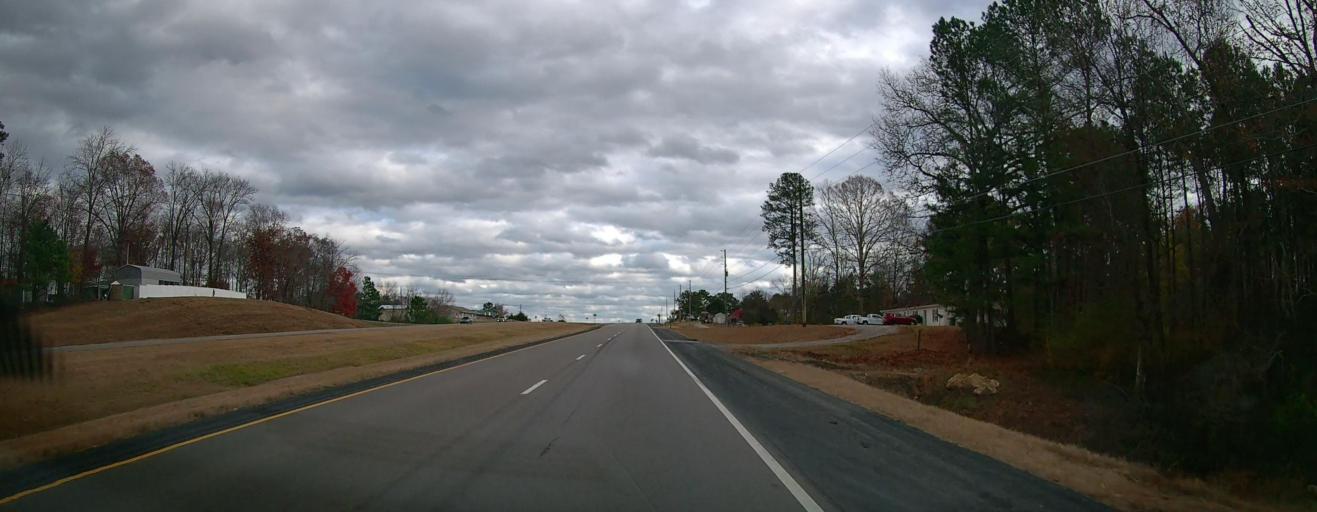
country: US
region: Alabama
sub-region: Morgan County
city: Falkville
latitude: 34.2546
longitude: -86.9750
